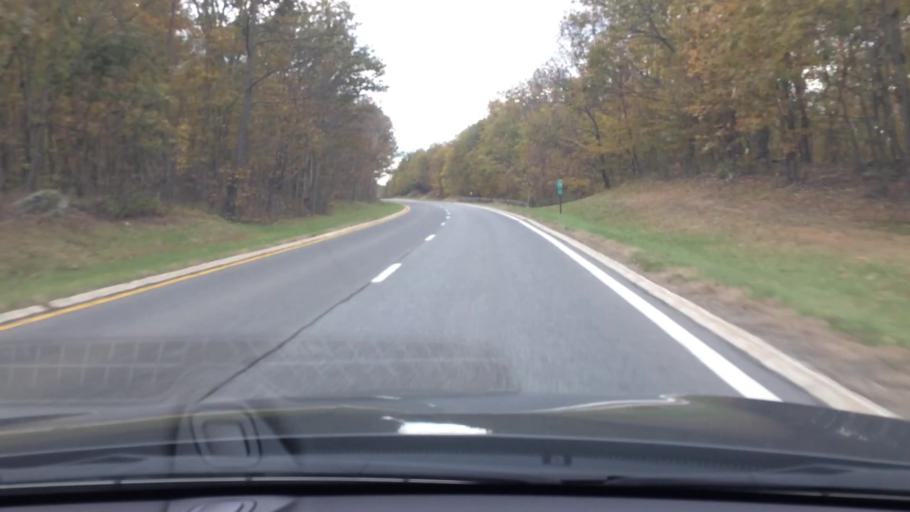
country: US
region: New York
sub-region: Dutchess County
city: Pine Plains
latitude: 42.0663
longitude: -73.7271
